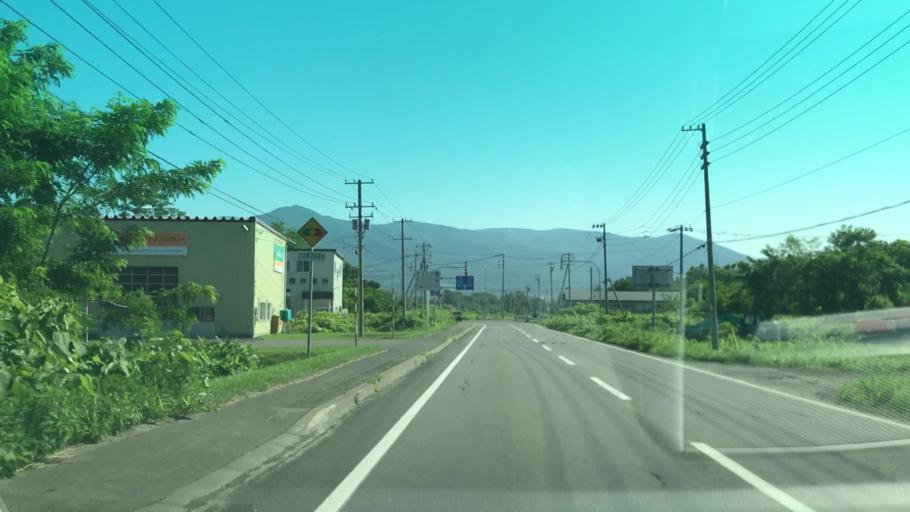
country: JP
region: Hokkaido
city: Iwanai
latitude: 43.0000
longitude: 140.5394
